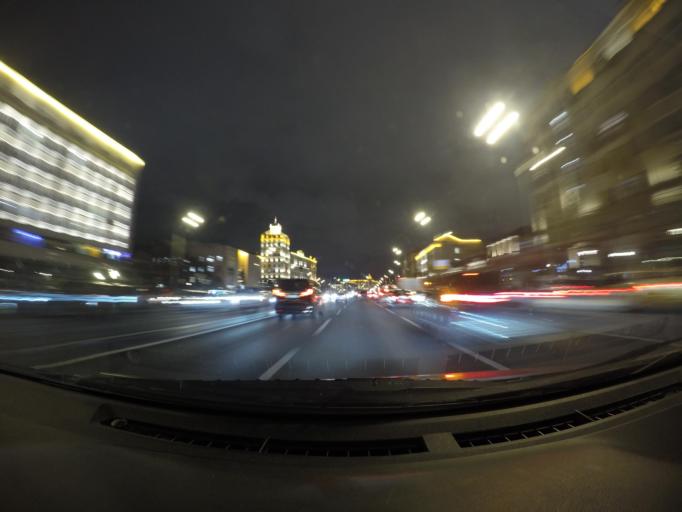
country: RU
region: Moscow
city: Moscow
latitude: 55.7734
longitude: 37.6127
